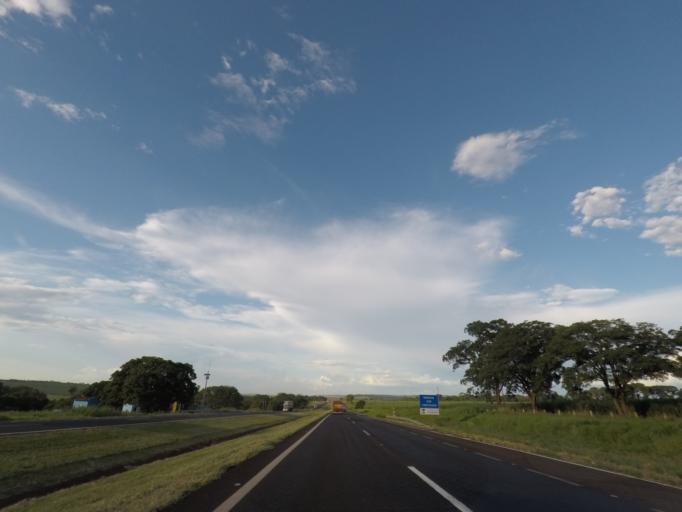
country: BR
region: Sao Paulo
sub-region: Ituverava
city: Ituverava
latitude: -20.3168
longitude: -47.8022
